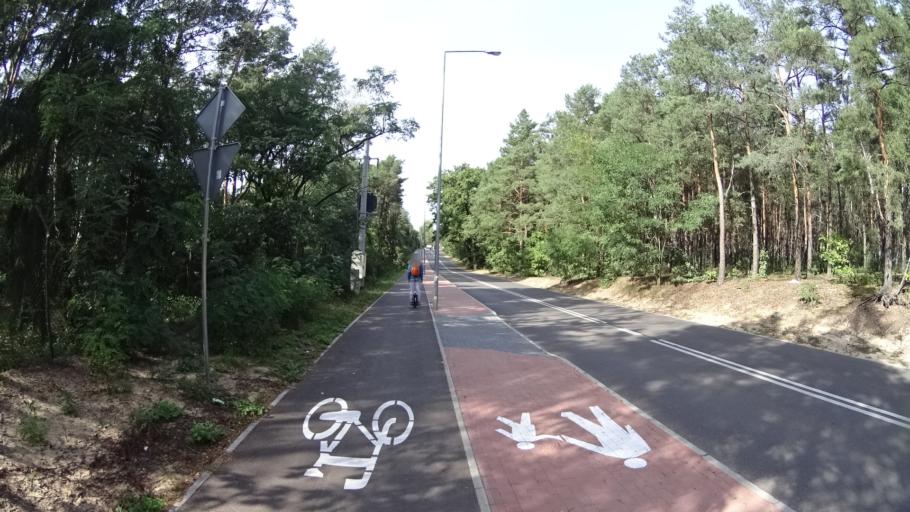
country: PL
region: Masovian Voivodeship
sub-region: Powiat legionowski
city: Bialobrzegi
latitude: 52.4621
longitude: 21.0777
